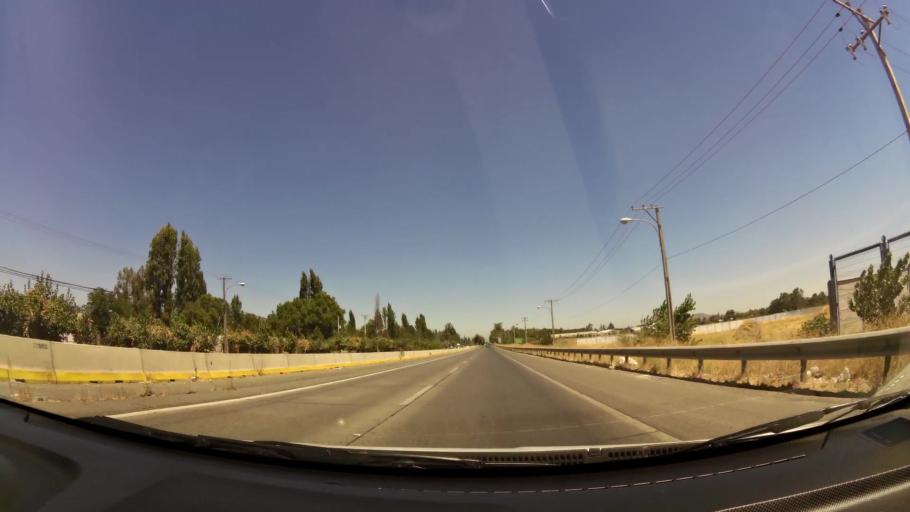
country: CL
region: O'Higgins
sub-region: Provincia de Cachapoal
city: Rancagua
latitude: -34.2199
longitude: -70.7764
